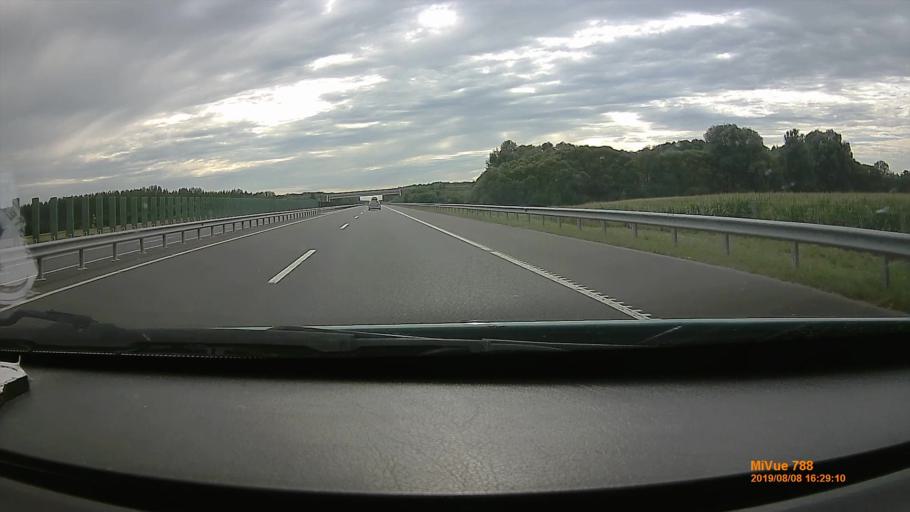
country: HU
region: Szabolcs-Szatmar-Bereg
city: Kantorjanosi
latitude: 47.9539
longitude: 22.1510
